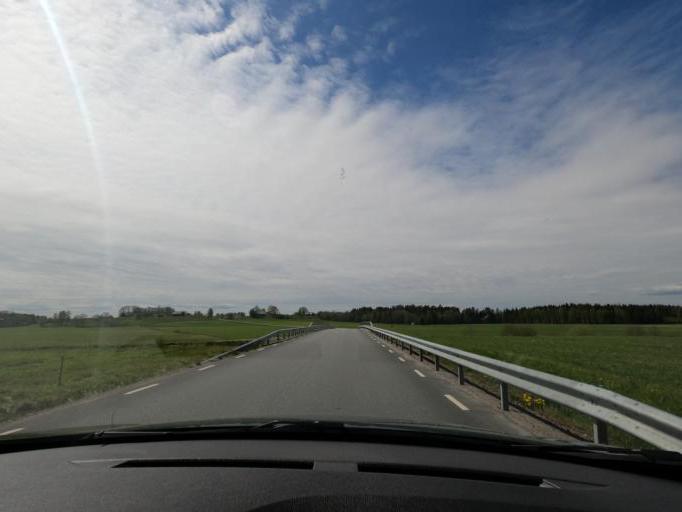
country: SE
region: Joenkoeping
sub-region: Varnamo Kommun
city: Bredaryd
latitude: 57.1297
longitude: 13.6888
